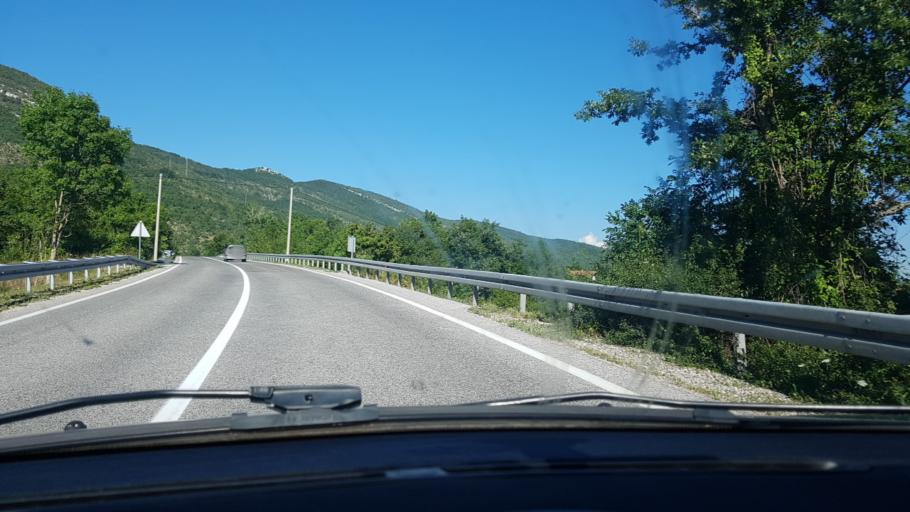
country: HR
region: Zadarska
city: Gracac
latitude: 44.3177
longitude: 15.7753
